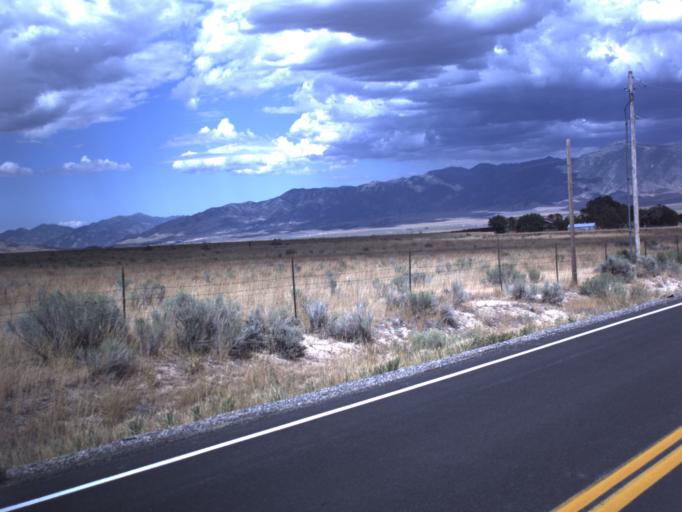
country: US
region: Utah
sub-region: Tooele County
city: Grantsville
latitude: 40.3362
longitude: -112.4913
